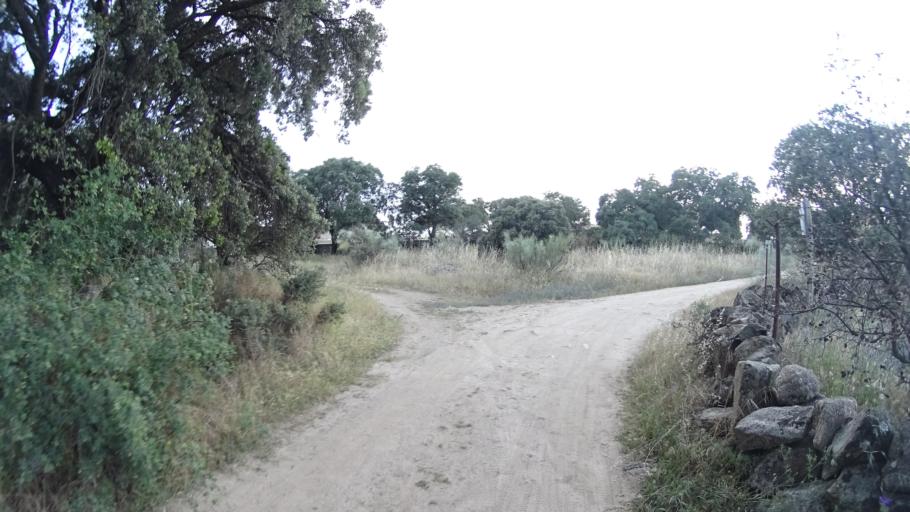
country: ES
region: Madrid
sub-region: Provincia de Madrid
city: Colmenarejo
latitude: 40.5350
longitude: -4.0067
